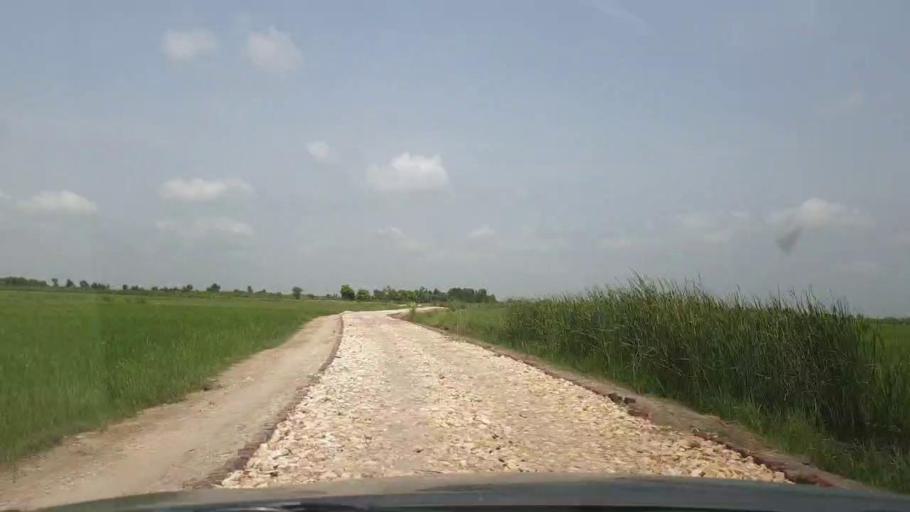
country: PK
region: Sindh
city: Ratodero
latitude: 27.9190
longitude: 68.3070
